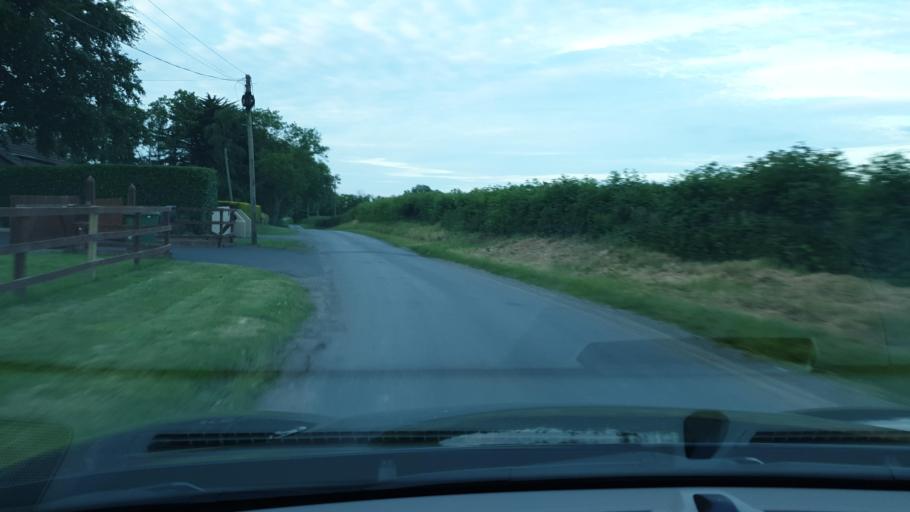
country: IE
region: Leinster
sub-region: An Mhi
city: Ashbourne
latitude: 53.4811
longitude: -6.3520
